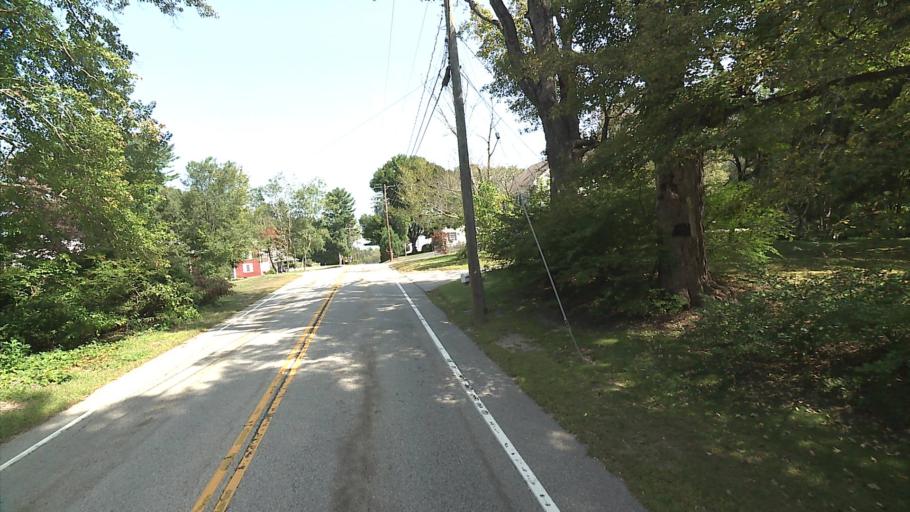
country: US
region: Connecticut
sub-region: Windham County
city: South Woodstock
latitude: 41.8998
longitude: -71.9611
